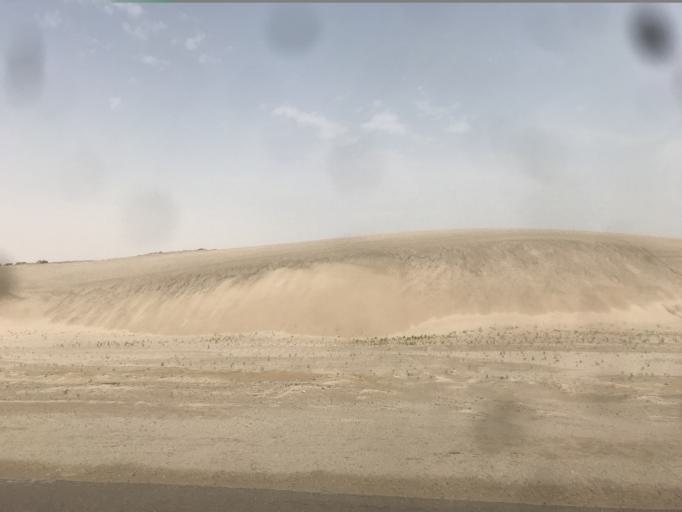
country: SA
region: Eastern Province
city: Abqaiq
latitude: 25.9057
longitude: 50.0113
